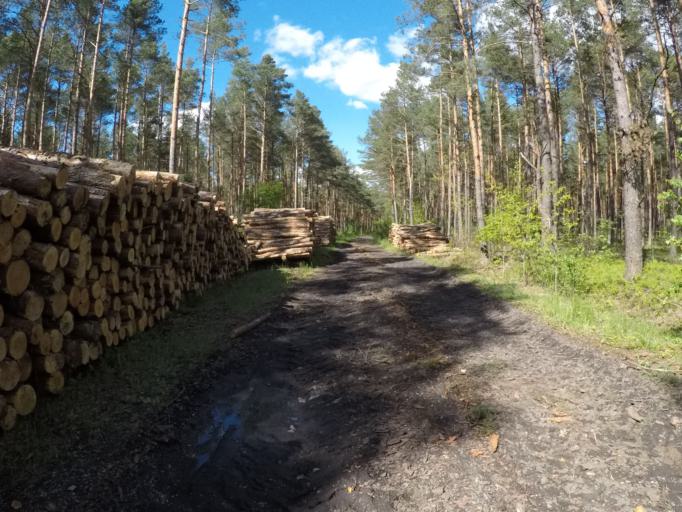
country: PL
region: Swietokrzyskie
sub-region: Powiat kielecki
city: Kostomloty Drugie
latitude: 50.8900
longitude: 20.5386
